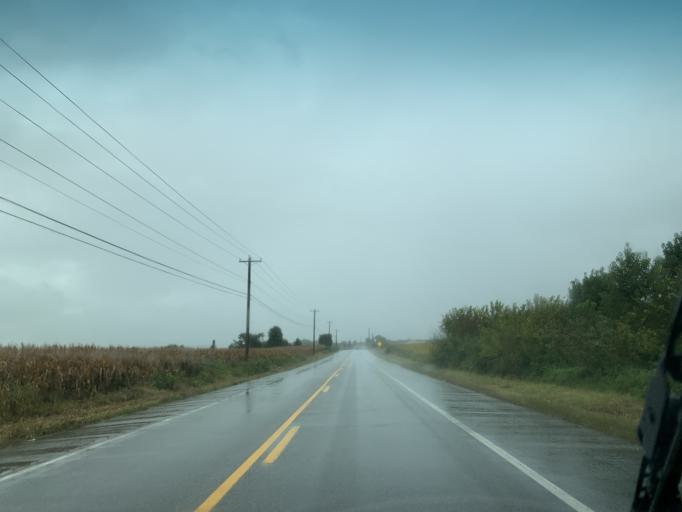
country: US
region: Maryland
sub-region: Queen Anne's County
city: Kingstown
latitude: 39.2084
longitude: -75.8637
